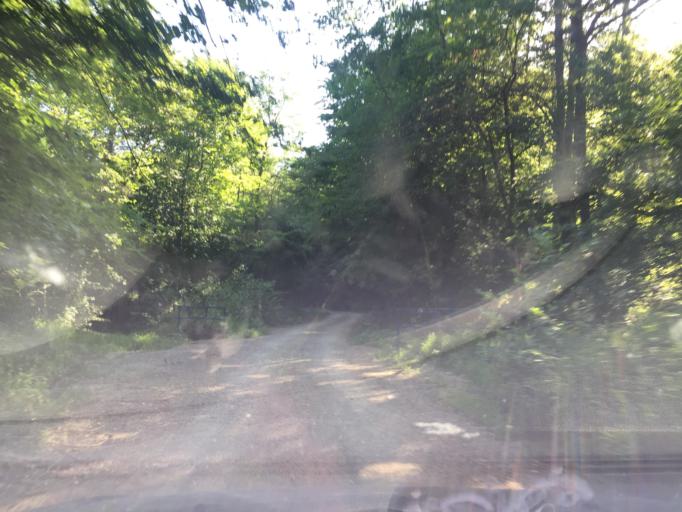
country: HR
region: Primorsko-Goranska
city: Klana
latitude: 45.4359
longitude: 14.3928
